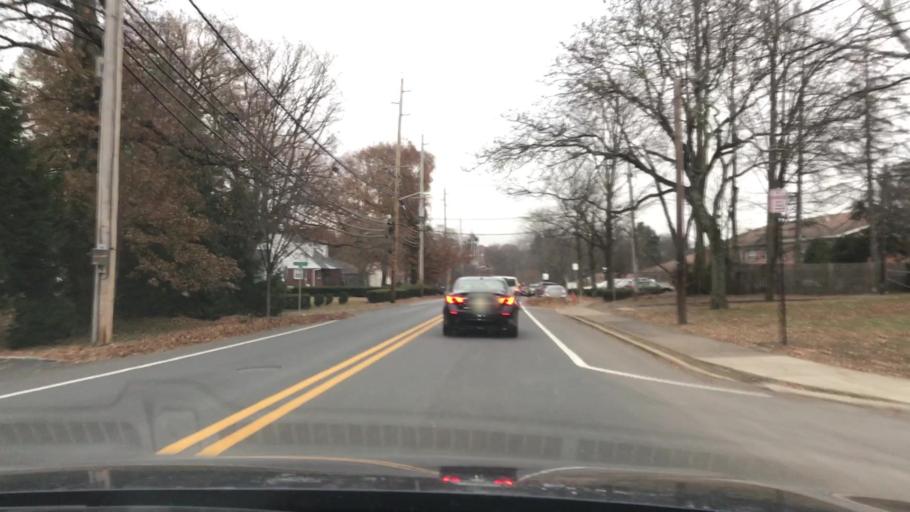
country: US
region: New Jersey
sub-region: Bergen County
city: Ho-Ho-Kus
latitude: 40.9713
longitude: -74.0883
